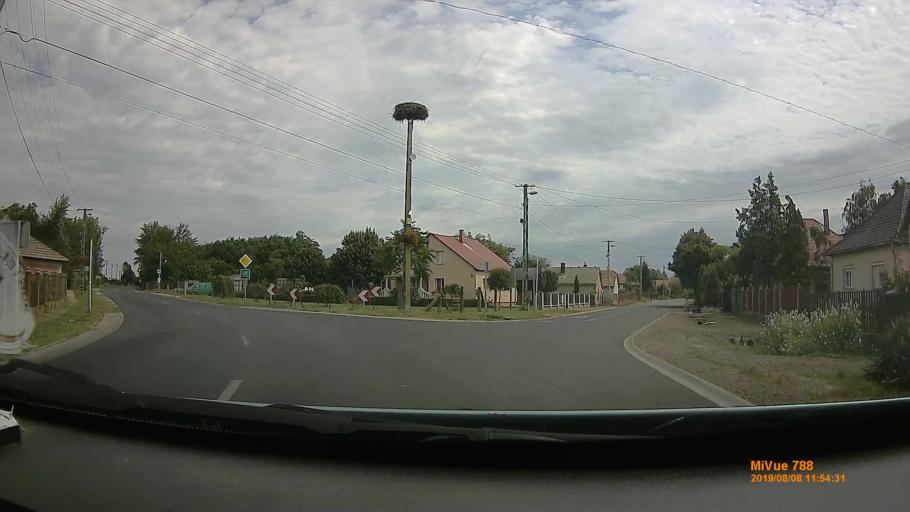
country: HU
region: Szabolcs-Szatmar-Bereg
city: Nyirmihalydi
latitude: 47.7349
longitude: 21.9711
